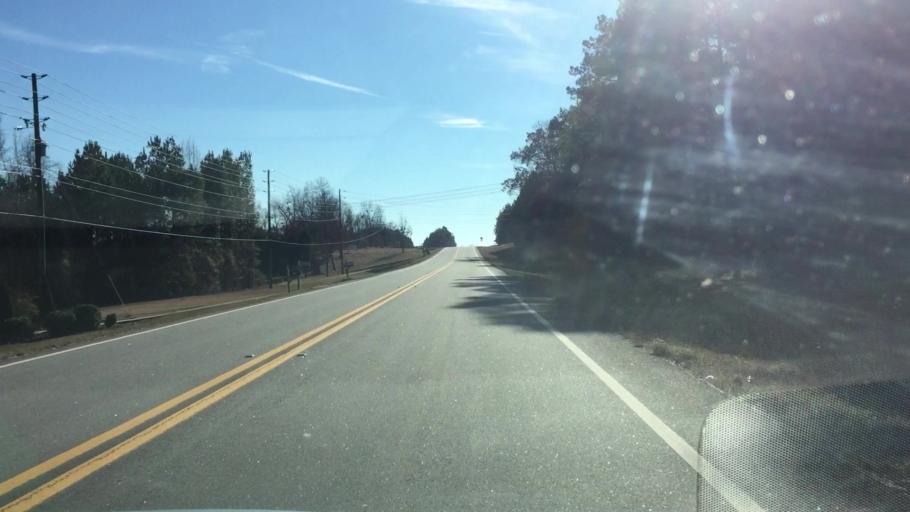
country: US
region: Georgia
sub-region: Newton County
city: Oakwood
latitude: 33.4682
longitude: -83.9662
